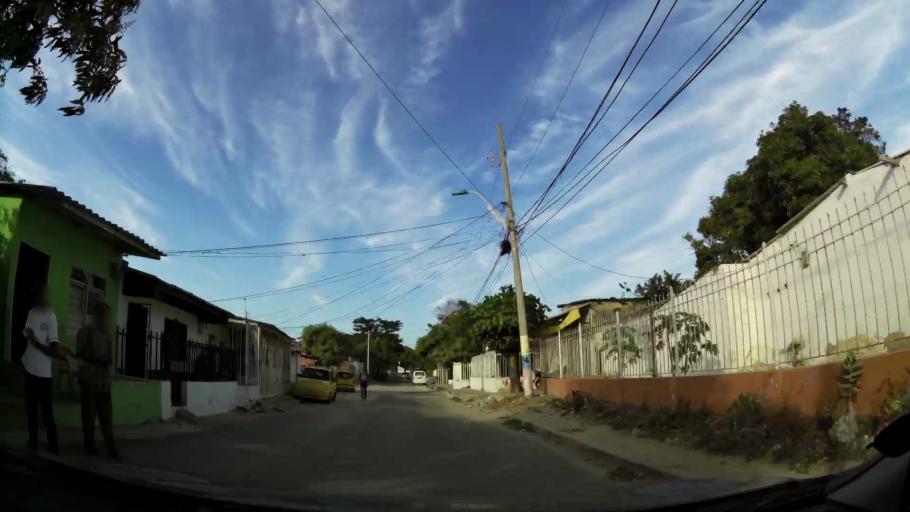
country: CO
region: Atlantico
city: Barranquilla
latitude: 10.9413
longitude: -74.8223
